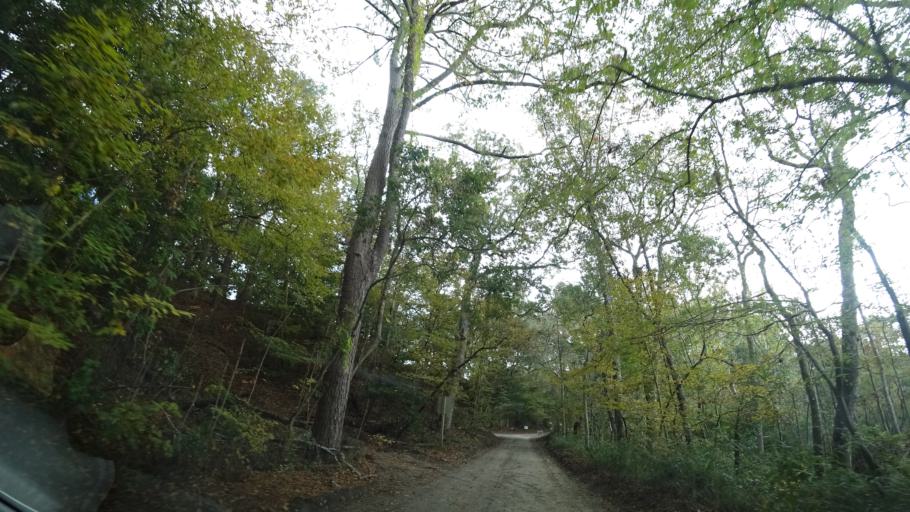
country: US
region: North Carolina
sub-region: Dare County
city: Kill Devil Hills
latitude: 35.9902
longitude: -75.6670
